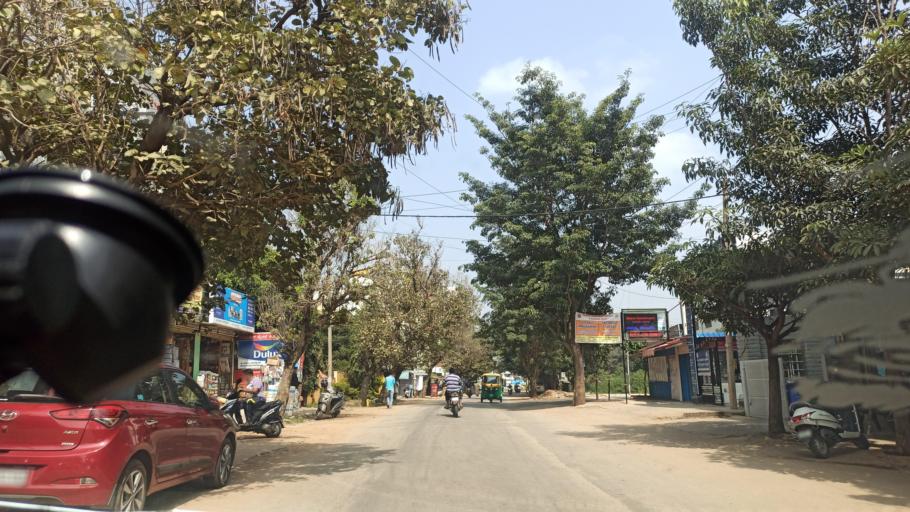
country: IN
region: Karnataka
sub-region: Bangalore Urban
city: Yelahanka
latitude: 13.0738
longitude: 77.6043
